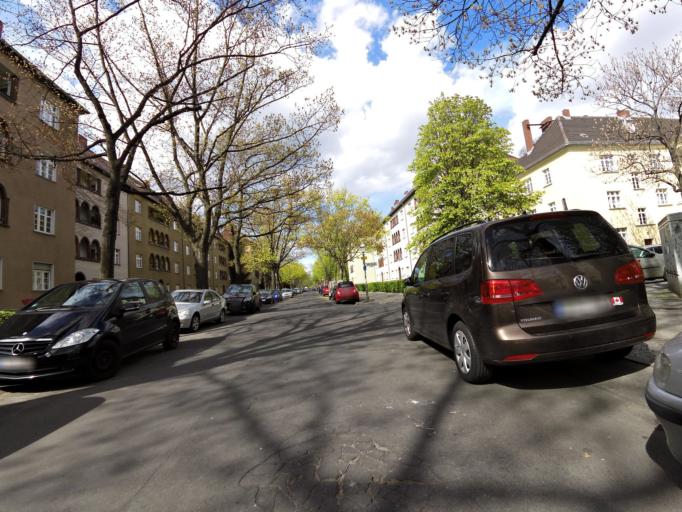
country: DE
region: Berlin
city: Schoneberg Bezirk
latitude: 52.4760
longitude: 13.3715
